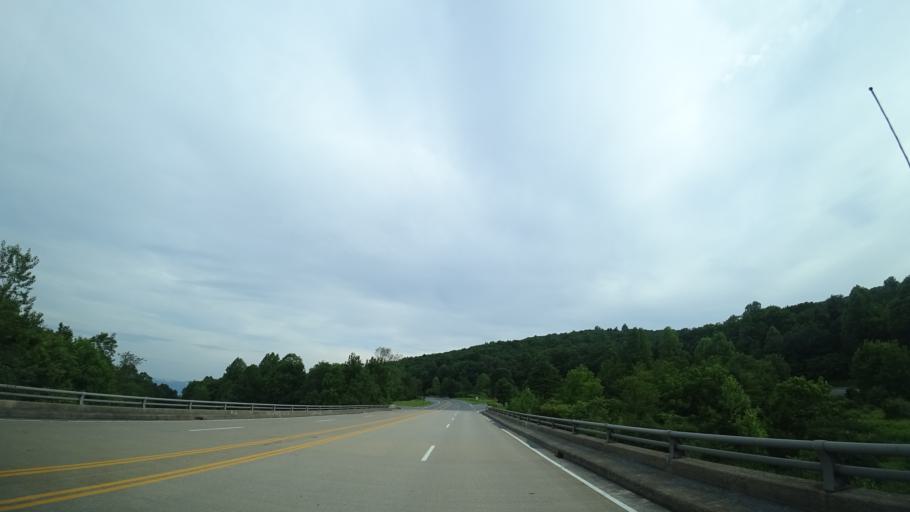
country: US
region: Virginia
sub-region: Page County
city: Luray
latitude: 38.6604
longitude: -78.3203
